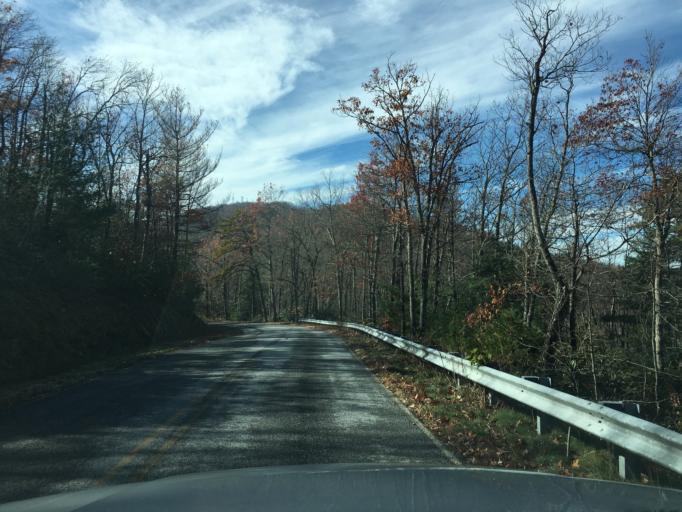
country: US
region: North Carolina
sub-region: Henderson County
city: Valley Hill
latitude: 35.2332
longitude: -82.5220
